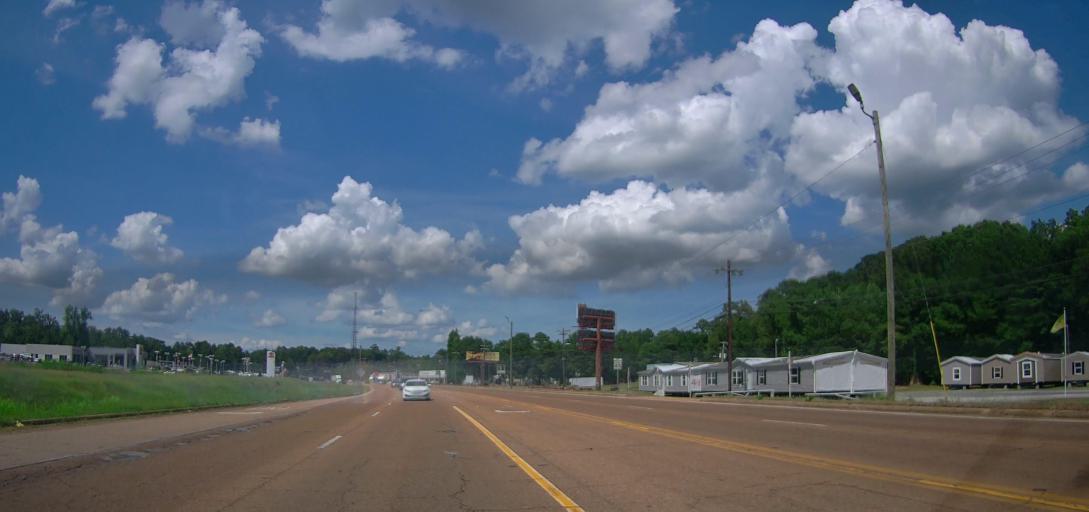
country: US
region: Mississippi
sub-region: Lowndes County
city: Columbus
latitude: 33.5468
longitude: -88.4344
